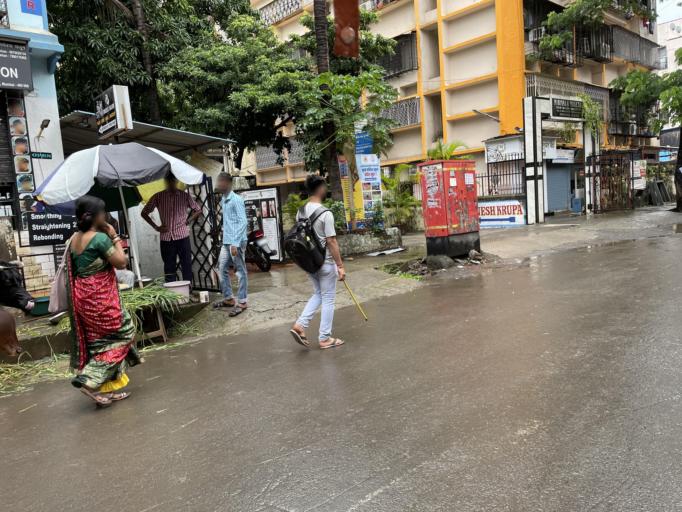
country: IN
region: Maharashtra
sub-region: Mumbai Suburban
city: Borivli
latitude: 19.2518
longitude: 72.8615
